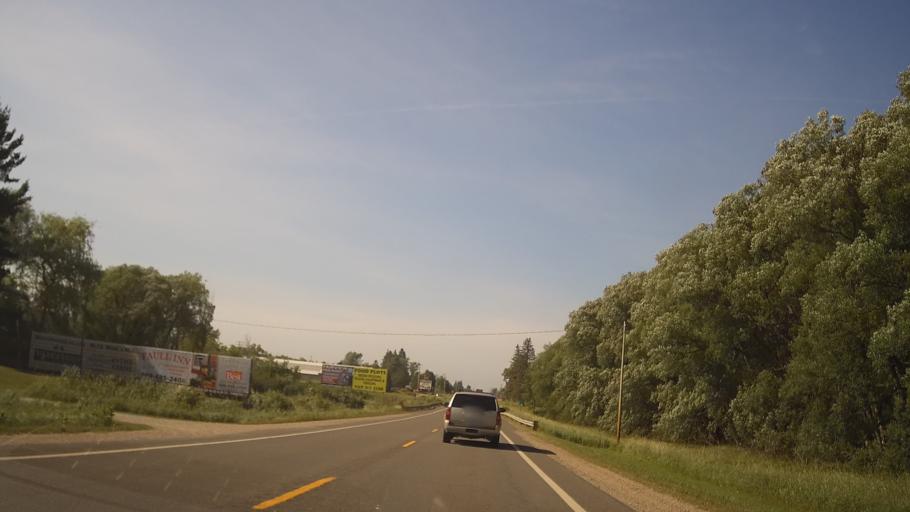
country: US
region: Michigan
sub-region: Ogemaw County
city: West Branch
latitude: 44.4038
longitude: -84.1164
